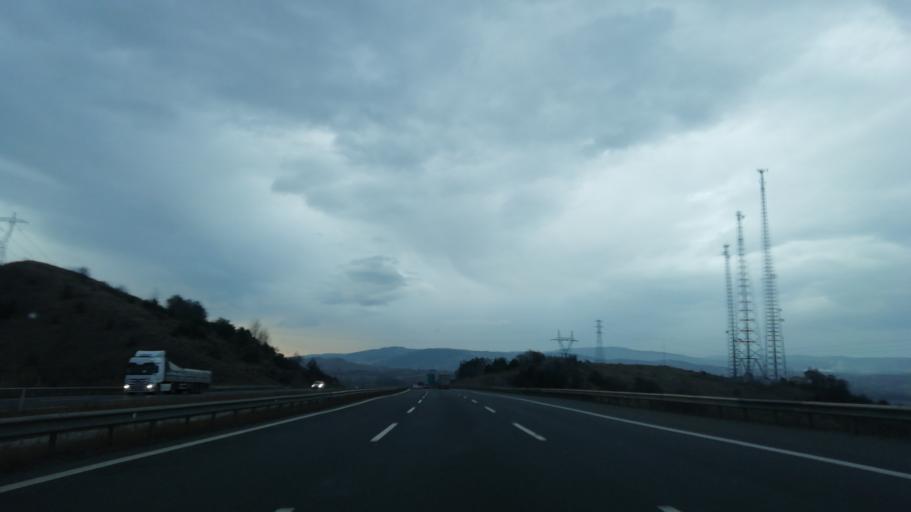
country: TR
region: Bolu
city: Yenicaga
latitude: 40.7655
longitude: 32.0333
